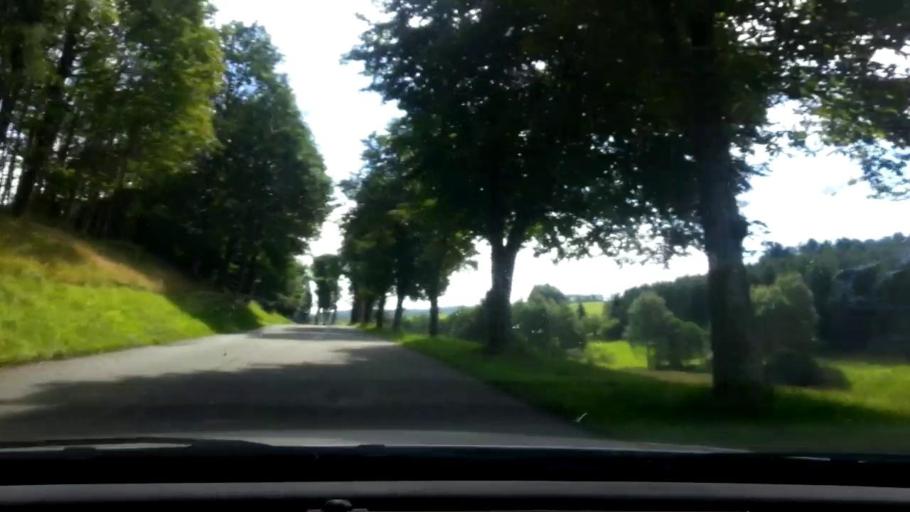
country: DE
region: Bavaria
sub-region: Upper Franconia
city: Bischofsgrun
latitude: 50.0547
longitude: 11.7840
